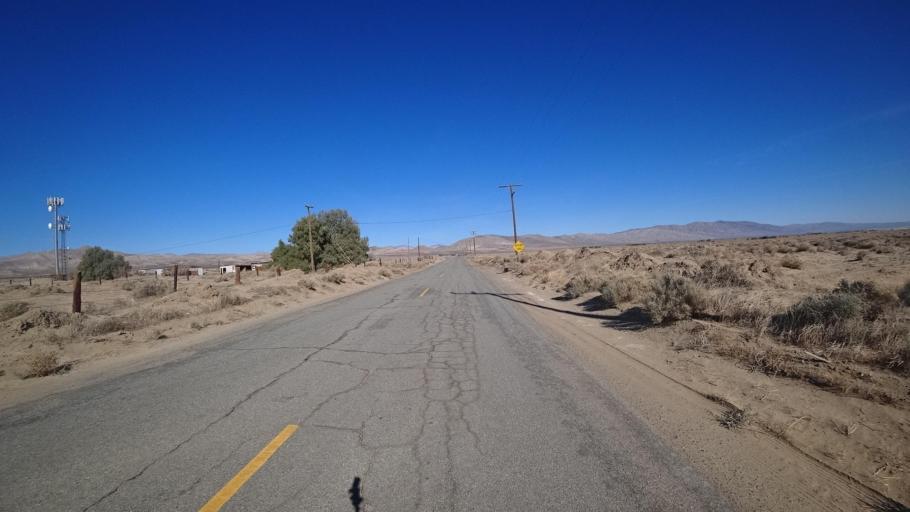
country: US
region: California
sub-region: Kern County
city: California City
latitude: 35.2882
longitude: -117.9679
